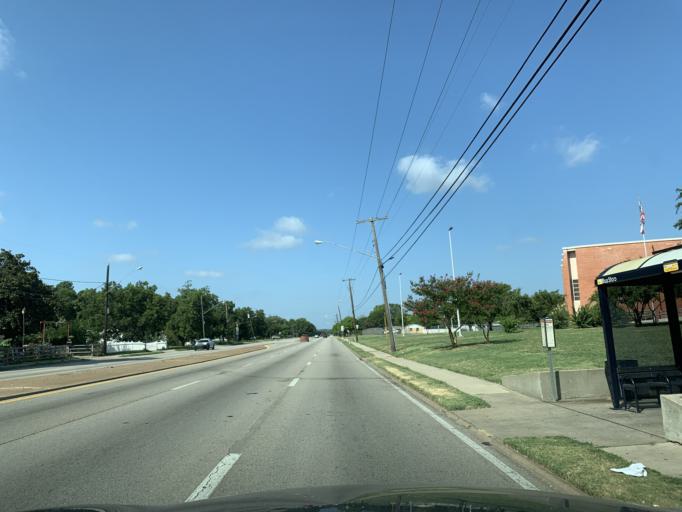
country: US
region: Texas
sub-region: Dallas County
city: Hutchins
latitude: 32.6904
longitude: -96.7811
